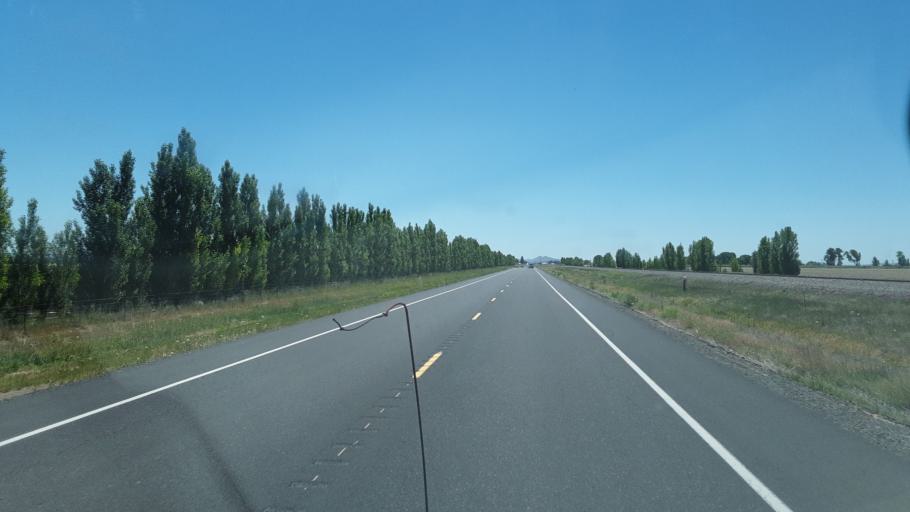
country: US
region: California
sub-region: Siskiyou County
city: Tulelake
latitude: 42.0172
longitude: -121.5398
